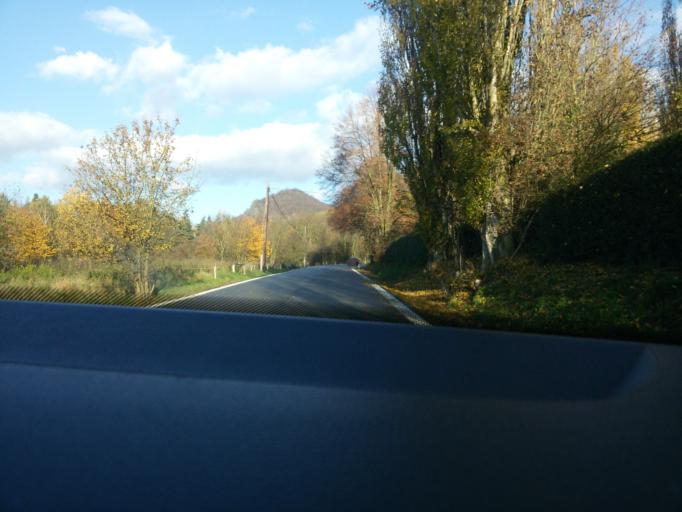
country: CZ
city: Doksy
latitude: 50.5292
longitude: 14.7231
